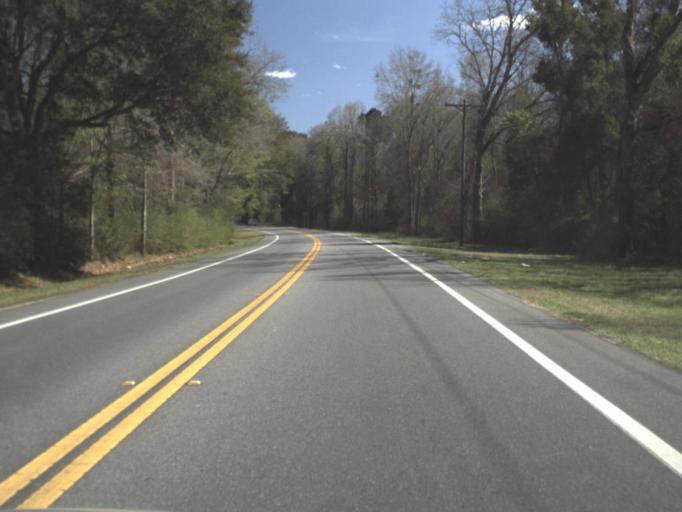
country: US
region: Florida
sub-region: Gadsden County
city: Gretna
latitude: 30.5945
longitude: -84.6469
